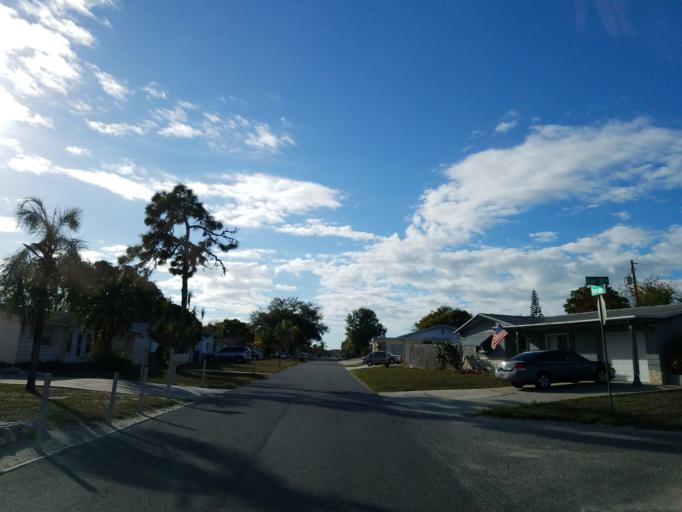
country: US
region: Florida
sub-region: Pasco County
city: Beacon Square
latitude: 28.2063
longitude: -82.7464
